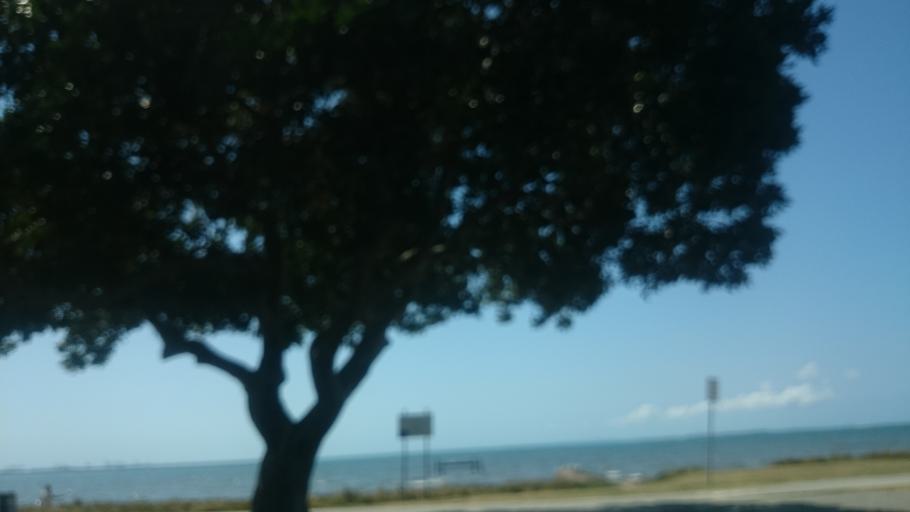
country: AU
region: Queensland
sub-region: Brisbane
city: Wynnum
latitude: -27.4455
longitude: 153.1814
